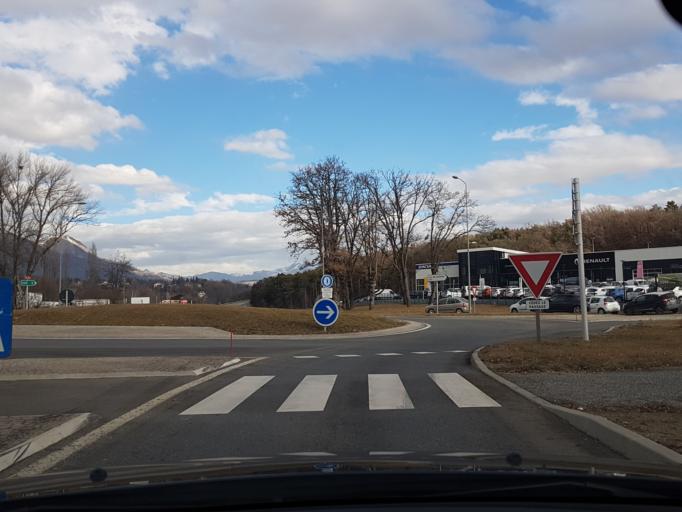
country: FR
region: Provence-Alpes-Cote d'Azur
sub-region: Departement des Hautes-Alpes
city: Tallard
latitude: 44.5099
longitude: 6.0459
